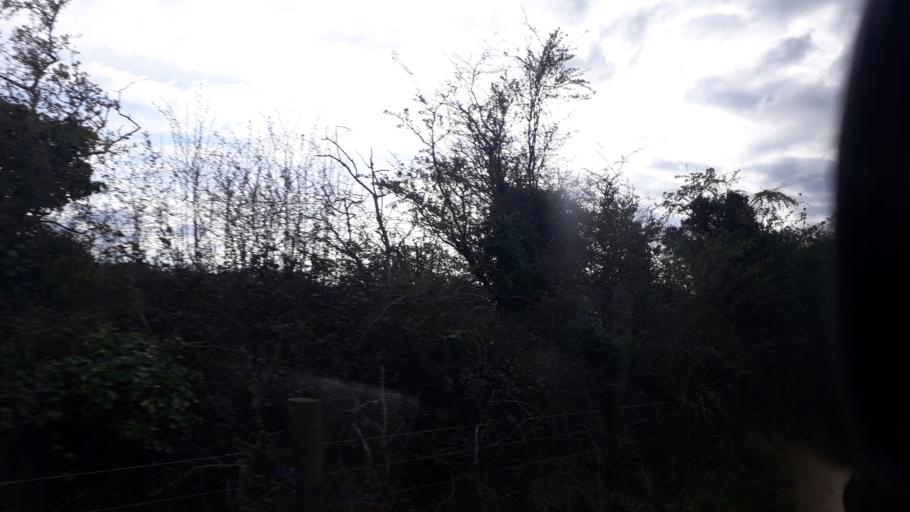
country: IE
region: Leinster
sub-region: An Iarmhi
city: An Muileann gCearr
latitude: 53.5069
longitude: -7.2972
